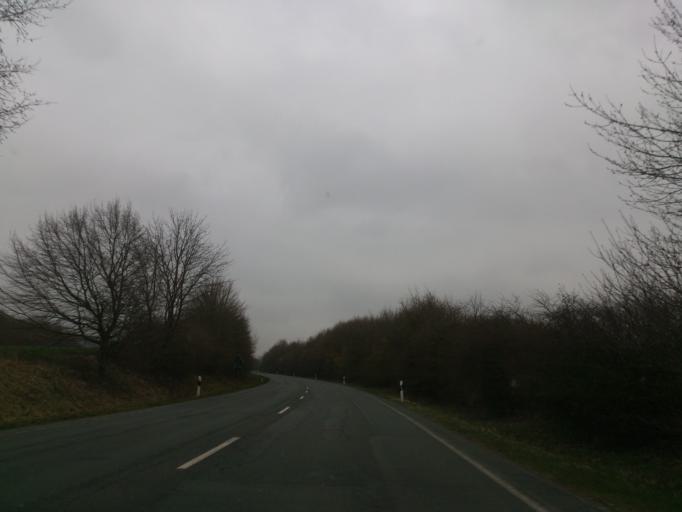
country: DE
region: North Rhine-Westphalia
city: Lichtenau
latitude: 51.5800
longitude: 8.8446
